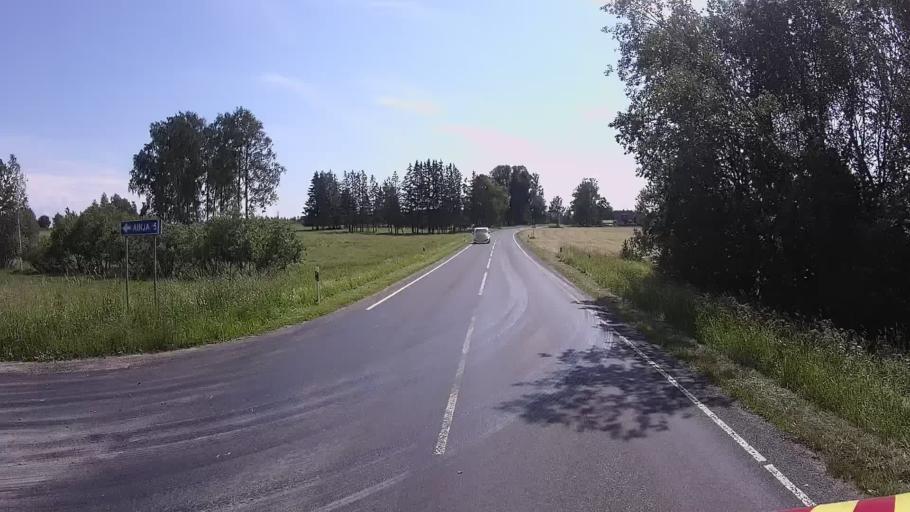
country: EE
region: Viljandimaa
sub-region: Karksi vald
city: Karksi-Nuia
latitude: 58.0600
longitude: 25.5507
